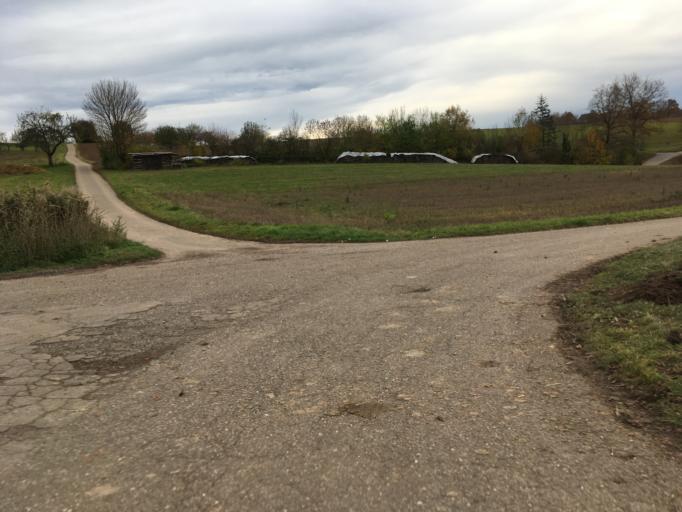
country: DE
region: Baden-Wuerttemberg
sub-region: Regierungsbezirk Stuttgart
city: Abstatt
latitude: 49.0888
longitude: 9.3016
